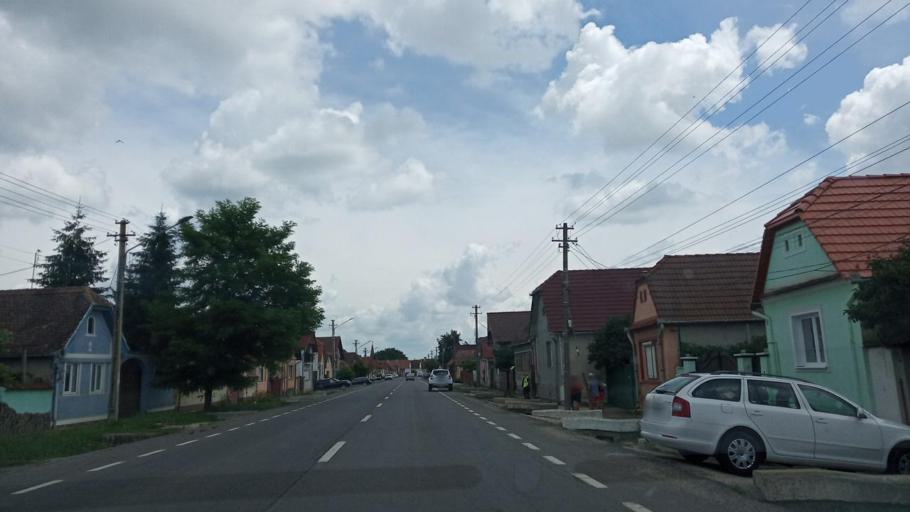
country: RO
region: Sibiu
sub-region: Comuna Cristian
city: Cristian
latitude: 45.7865
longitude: 24.0165
